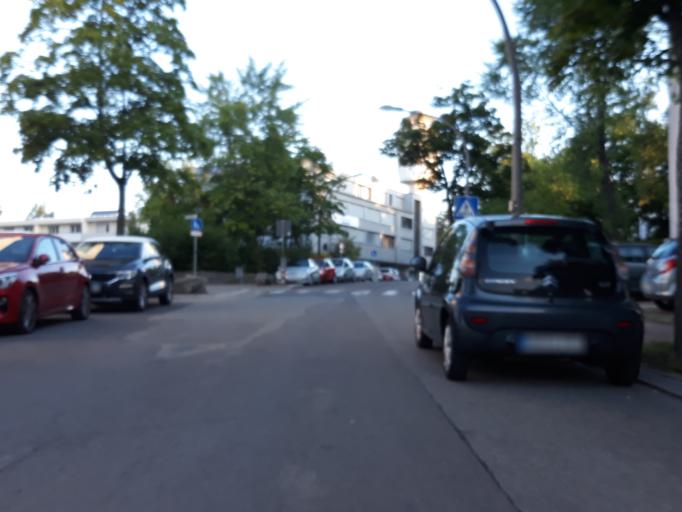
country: DE
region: Baden-Wuerttemberg
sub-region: Regierungsbezirk Stuttgart
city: Sindelfingen
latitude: 48.6992
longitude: 9.0182
